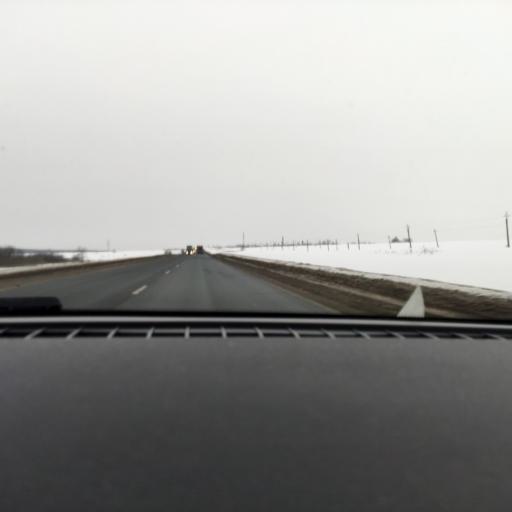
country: RU
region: Samara
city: Smyshlyayevka
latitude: 53.2888
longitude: 50.4607
